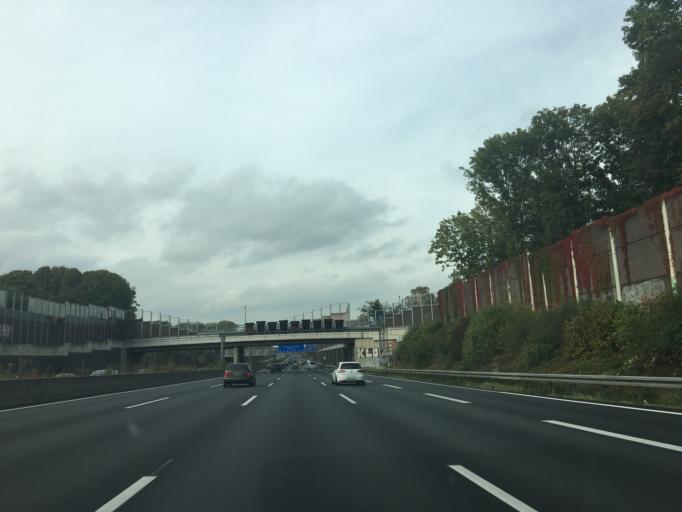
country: DE
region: North Rhine-Westphalia
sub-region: Regierungsbezirk Koln
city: Buchheim
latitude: 50.9604
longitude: 7.0338
